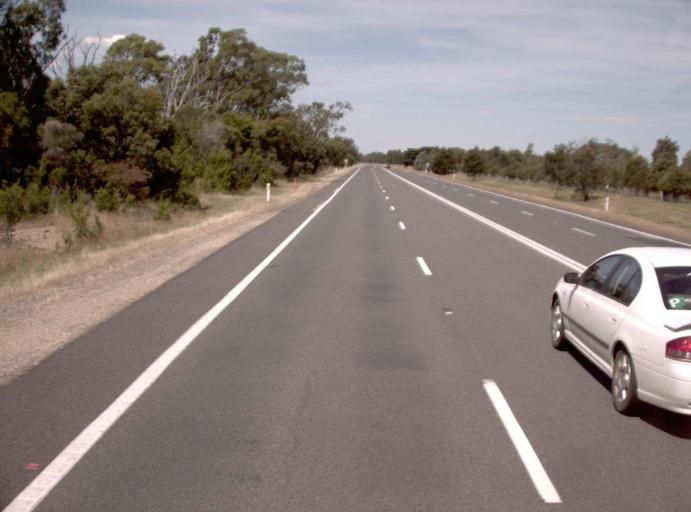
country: AU
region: Victoria
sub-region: East Gippsland
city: Bairnsdale
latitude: -37.8608
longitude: 147.5149
